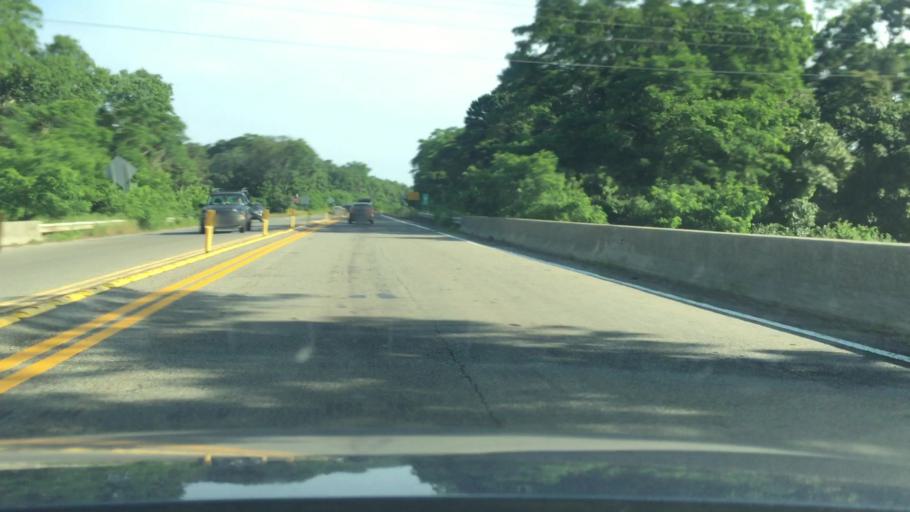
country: US
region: Massachusetts
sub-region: Barnstable County
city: Orleans
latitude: 41.7781
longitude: -70.0034
